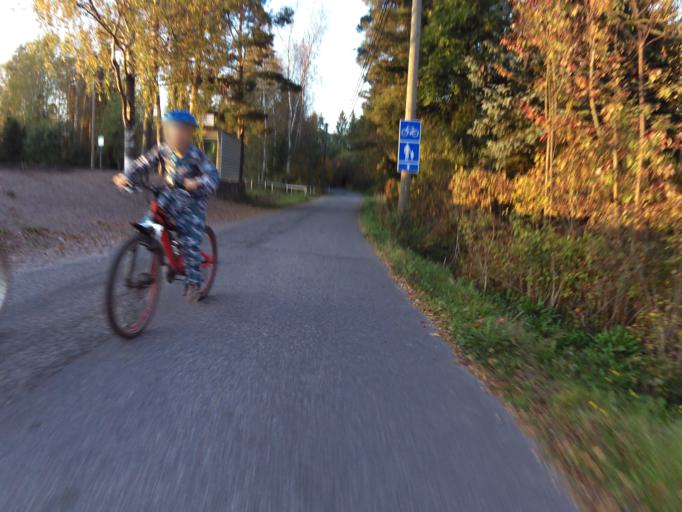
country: FI
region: Uusimaa
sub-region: Helsinki
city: Kilo
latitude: 60.2788
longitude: 24.7500
